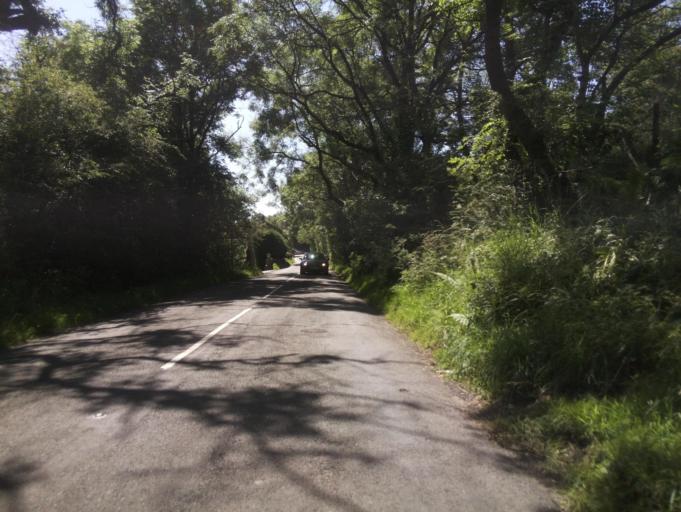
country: GB
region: England
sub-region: Derbyshire
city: Buxton
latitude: 53.1918
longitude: -1.8788
